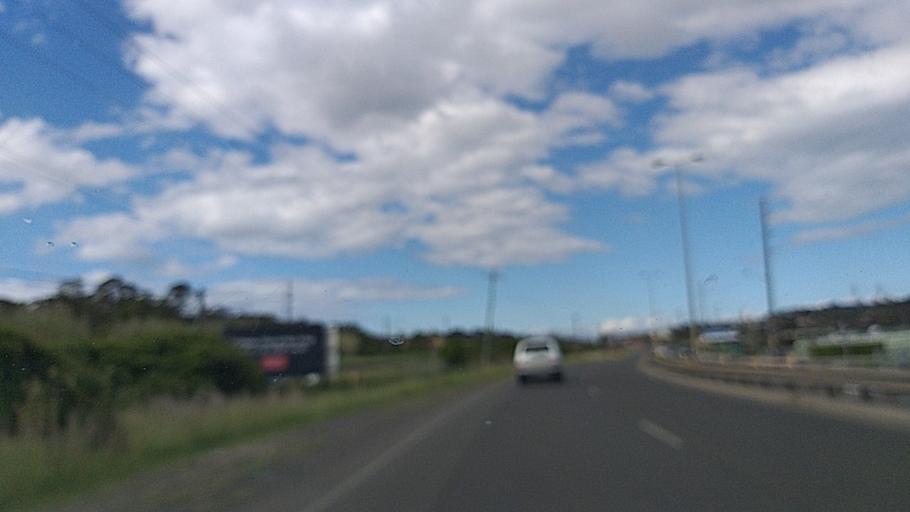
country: AU
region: New South Wales
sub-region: Wollongong
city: Berkeley
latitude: -34.4700
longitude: 150.8191
